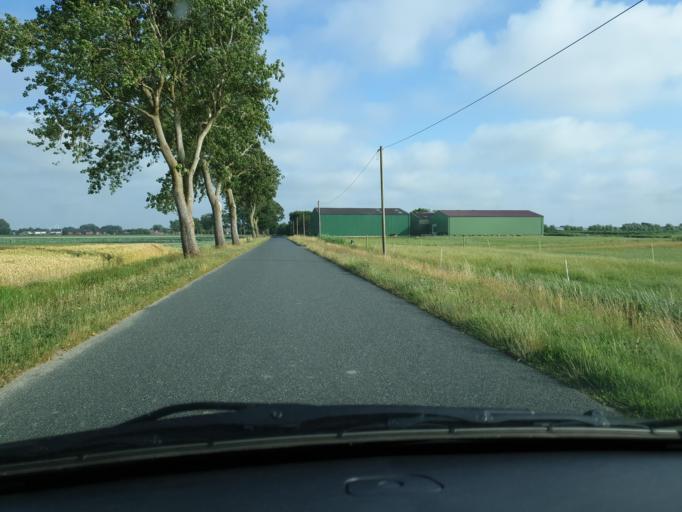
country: DE
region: Schleswig-Holstein
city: Friedrichskoog
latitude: 54.0118
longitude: 8.8647
